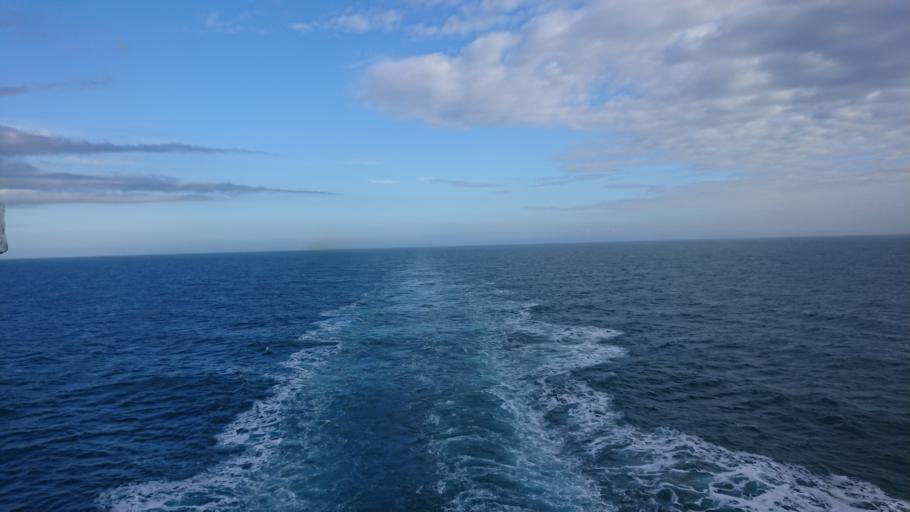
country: GB
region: Wales
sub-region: Pembrokeshire
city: Saint David's
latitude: 52.1362
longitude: -5.6248
